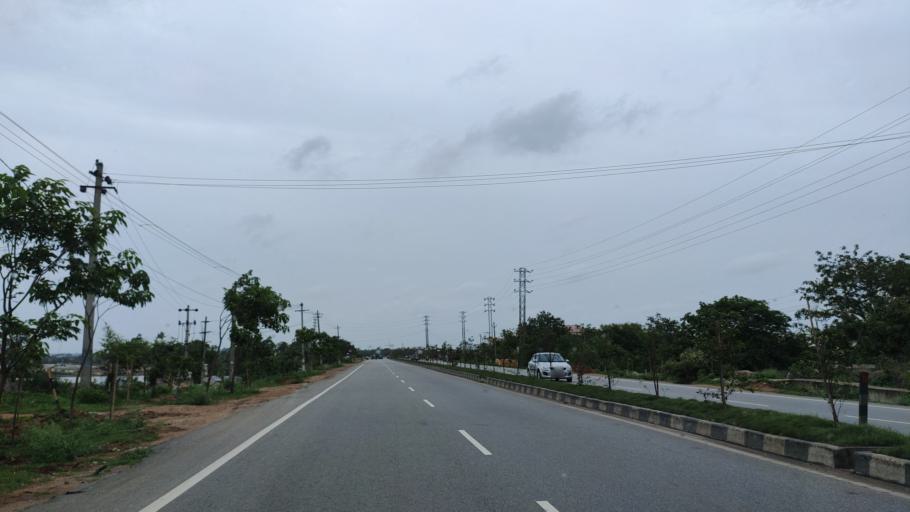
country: IN
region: Telangana
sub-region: Rangareddi
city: Secunderabad
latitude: 17.6041
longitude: 78.5681
